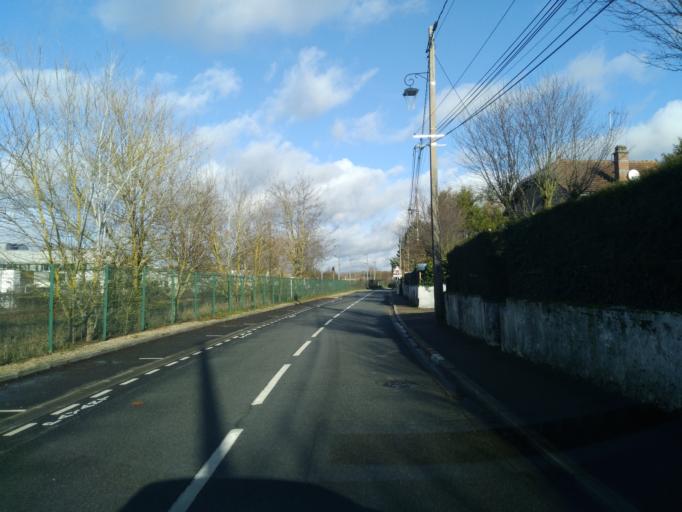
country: FR
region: Ile-de-France
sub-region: Departement des Yvelines
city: Villiers-Saint-Frederic
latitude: 48.8167
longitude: 1.8791
